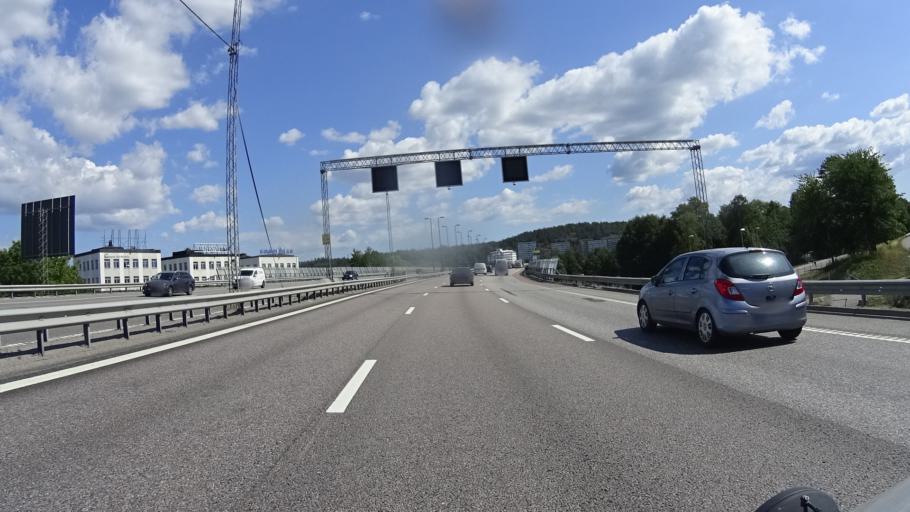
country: SE
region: Stockholm
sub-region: Botkyrka Kommun
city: Fittja
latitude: 59.2552
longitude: 17.8670
